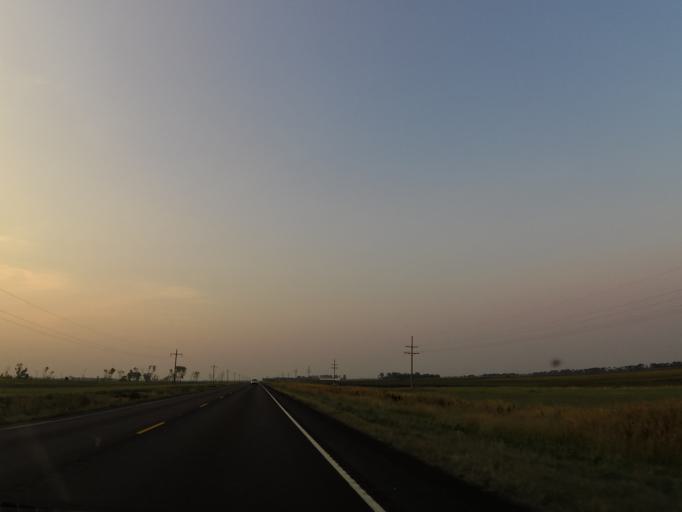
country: US
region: North Dakota
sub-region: Walsh County
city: Park River
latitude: 48.2112
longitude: -97.6226
